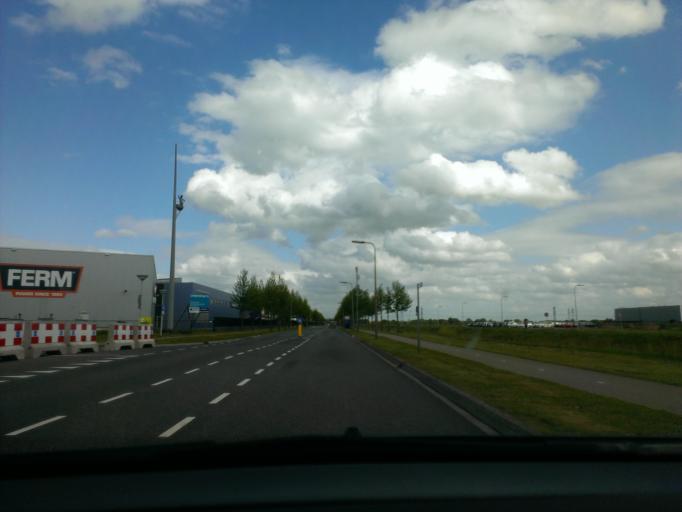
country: NL
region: Overijssel
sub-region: Gemeente Zwolle
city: Zwolle
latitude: 52.5311
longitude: 6.1645
